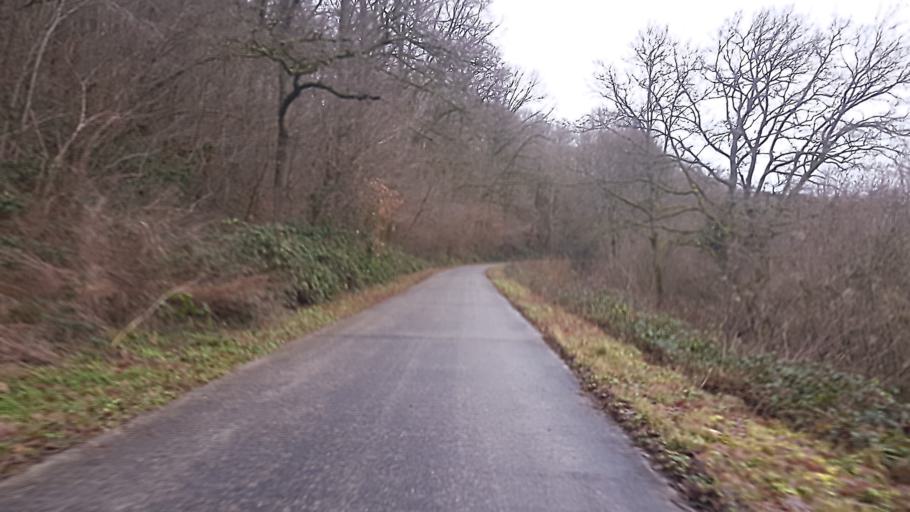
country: BE
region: Wallonia
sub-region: Province de Namur
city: Couvin
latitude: 50.0645
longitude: 4.5987
